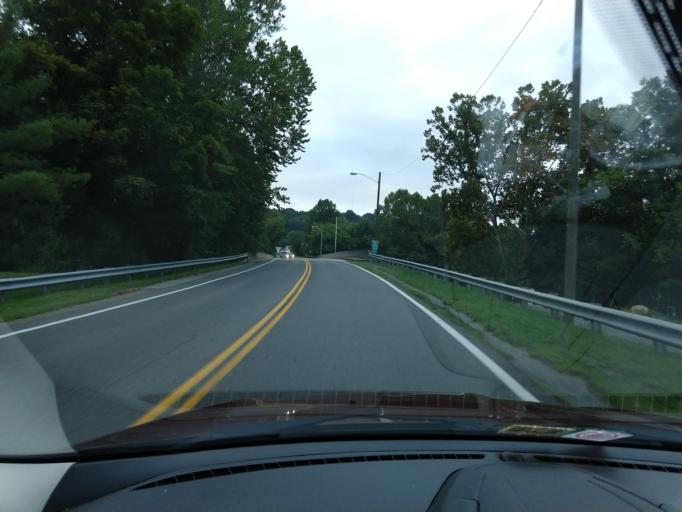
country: US
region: Virginia
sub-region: City of Covington
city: Fairlawn
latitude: 37.7558
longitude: -79.9869
